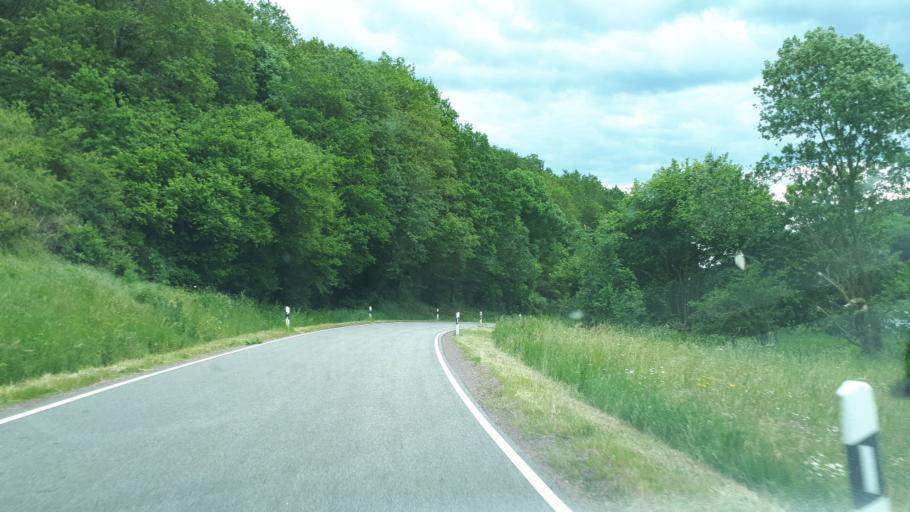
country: DE
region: Rheinland-Pfalz
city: Immerath
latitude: 50.1331
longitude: 6.9512
